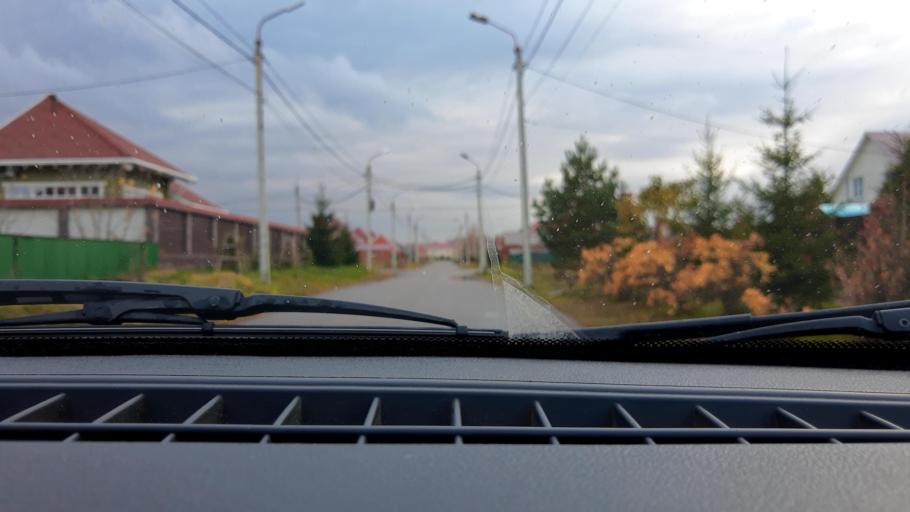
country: RU
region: Bashkortostan
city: Ufa
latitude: 54.8553
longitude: 56.0165
